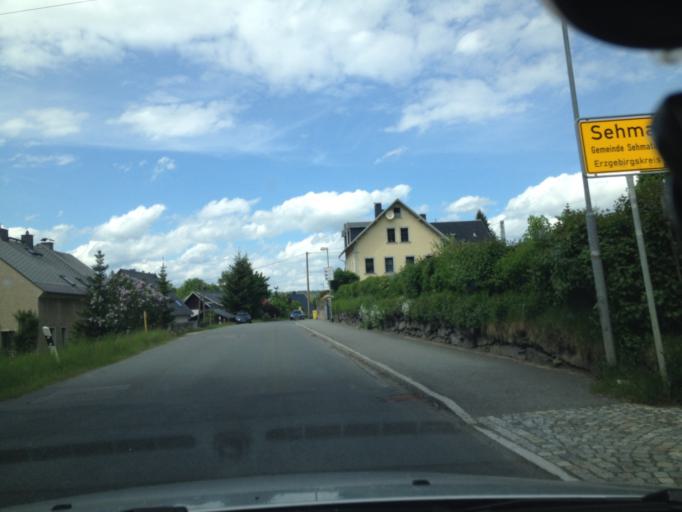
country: DE
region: Saxony
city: Barenstein
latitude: 50.5237
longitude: 12.9960
